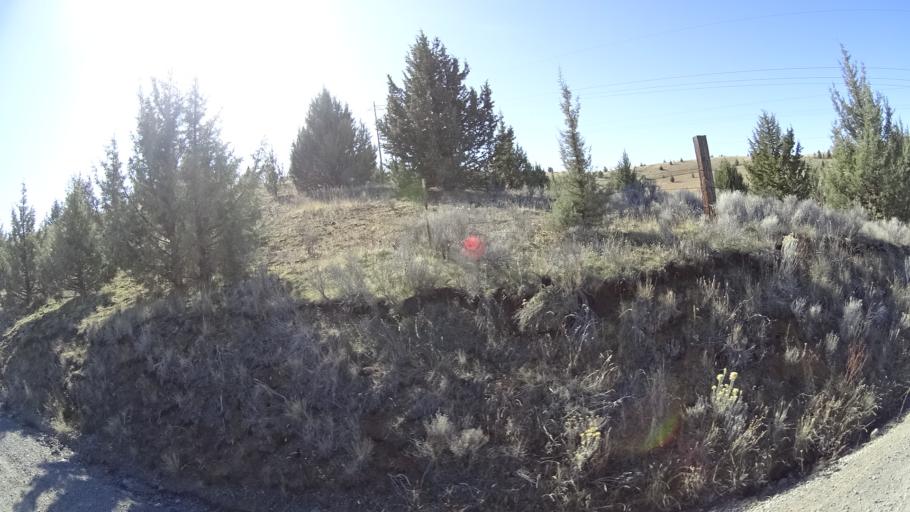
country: US
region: California
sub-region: Siskiyou County
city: Montague
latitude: 41.7767
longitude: -122.3584
